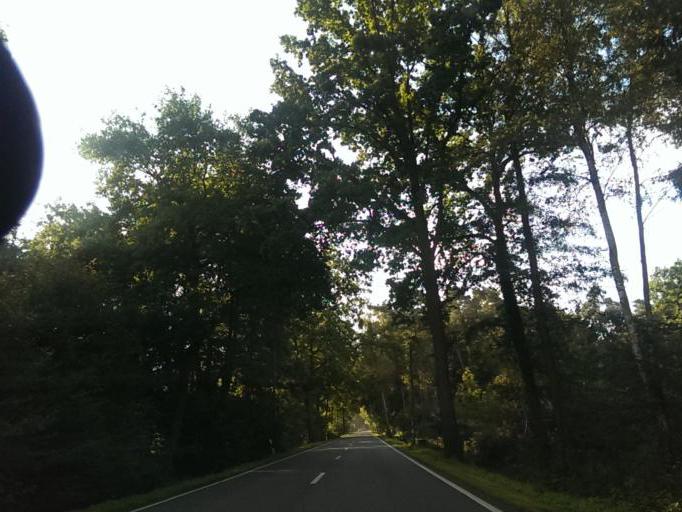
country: DE
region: Lower Saxony
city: Garbsen-Mitte
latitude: 52.5236
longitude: 9.6209
